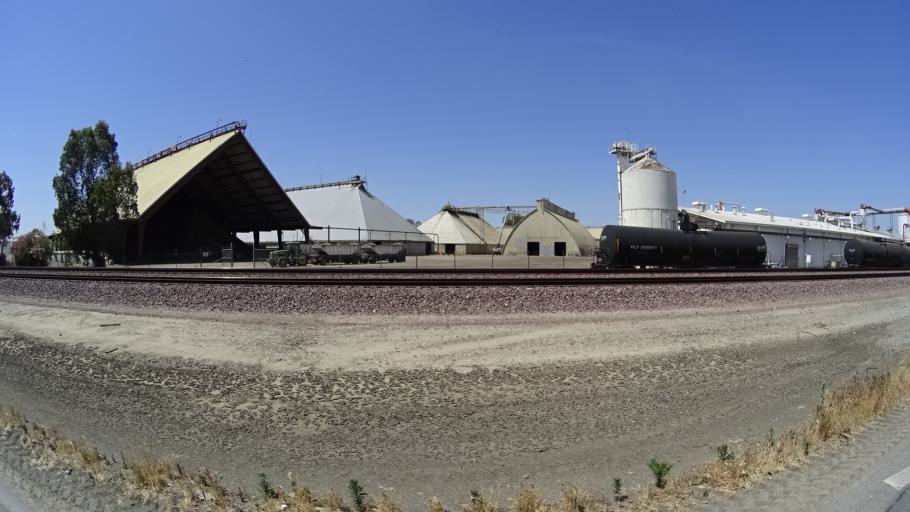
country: US
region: California
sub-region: Kings County
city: Corcoran
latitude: 36.0916
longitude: -119.5517
